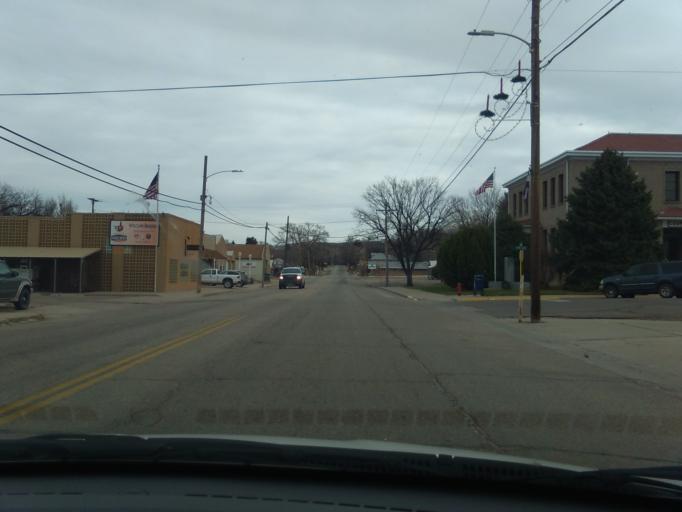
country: US
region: Colorado
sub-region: Yuma County
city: Wray
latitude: 40.0789
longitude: -102.2211
